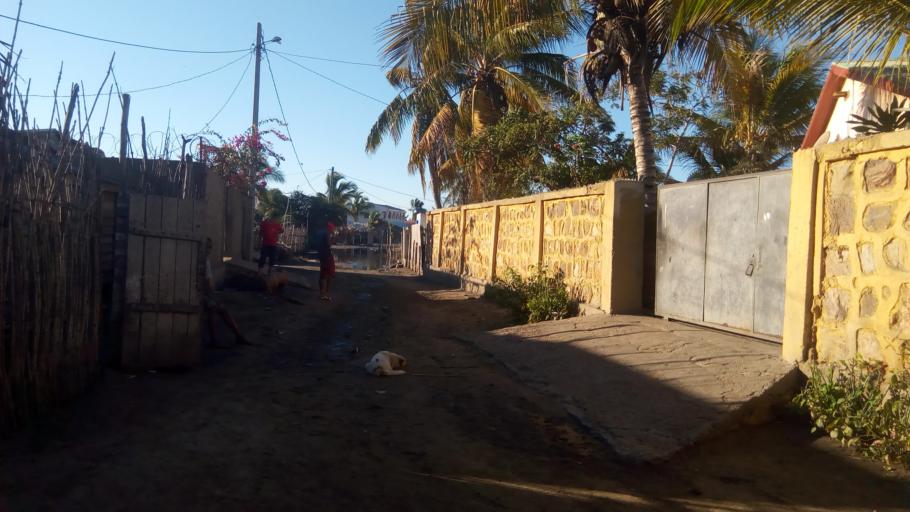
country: MG
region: Menabe
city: Morondava
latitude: -20.2978
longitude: 44.2780
